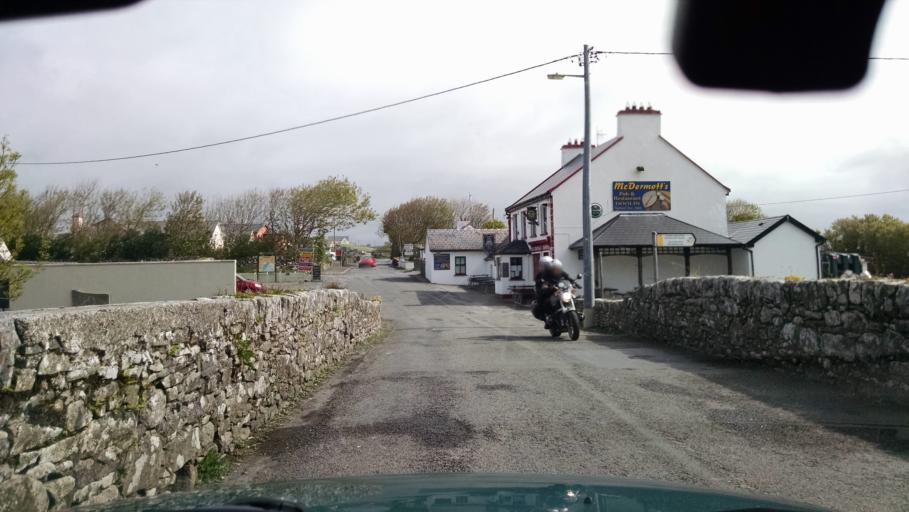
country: IE
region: Connaught
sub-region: County Galway
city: Bearna
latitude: 53.0187
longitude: -9.3717
